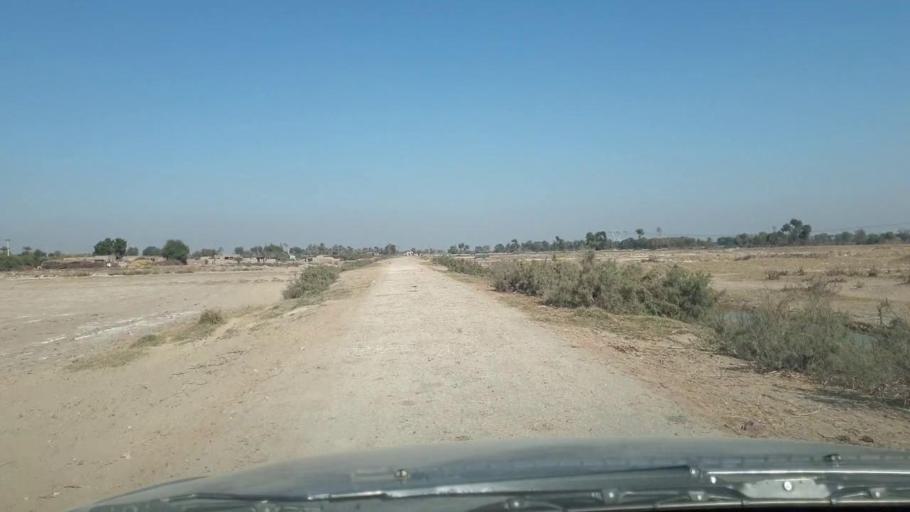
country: PK
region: Sindh
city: Adilpur
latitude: 27.8831
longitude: 69.2723
